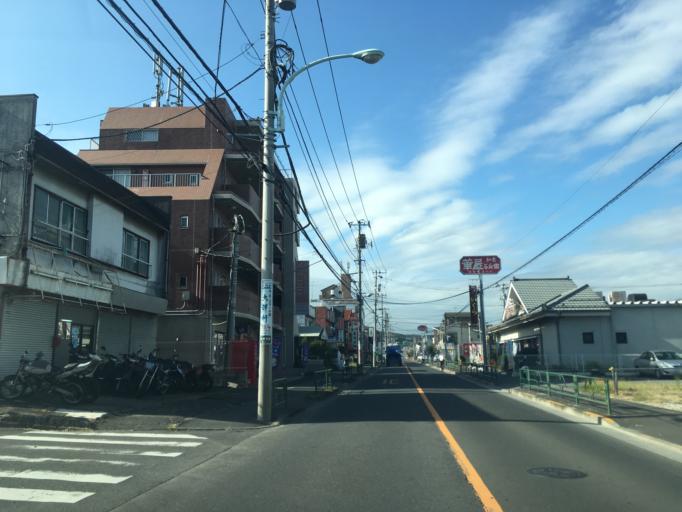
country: JP
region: Tokyo
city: Hino
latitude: 35.6562
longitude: 139.3961
